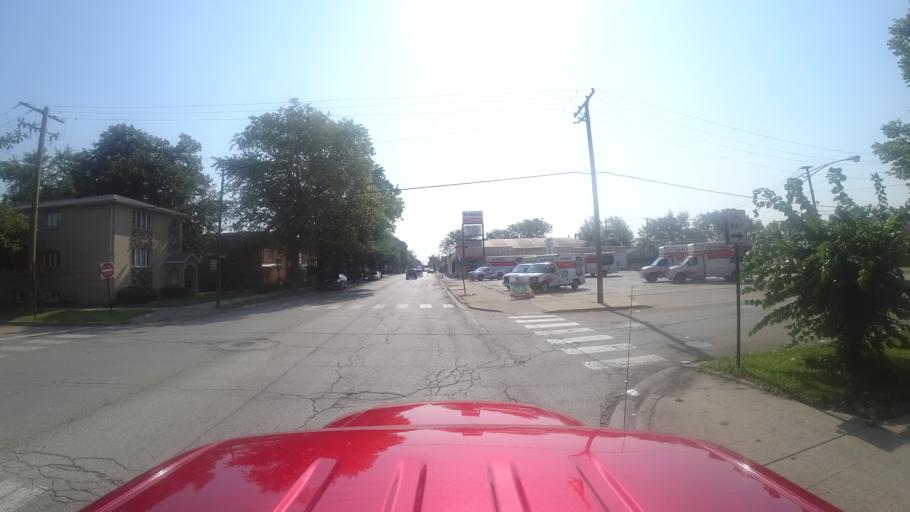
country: US
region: Illinois
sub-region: Cook County
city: Cicero
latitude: 41.8076
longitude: -87.7422
